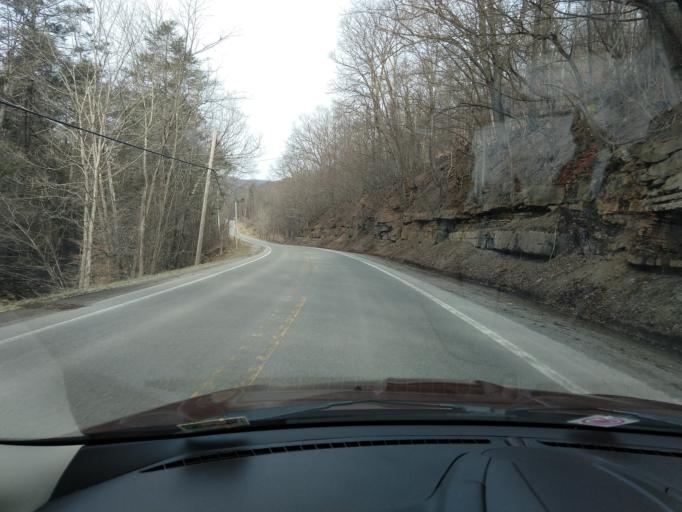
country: US
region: West Virginia
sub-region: Tucker County
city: Parsons
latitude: 38.9067
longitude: -79.4953
